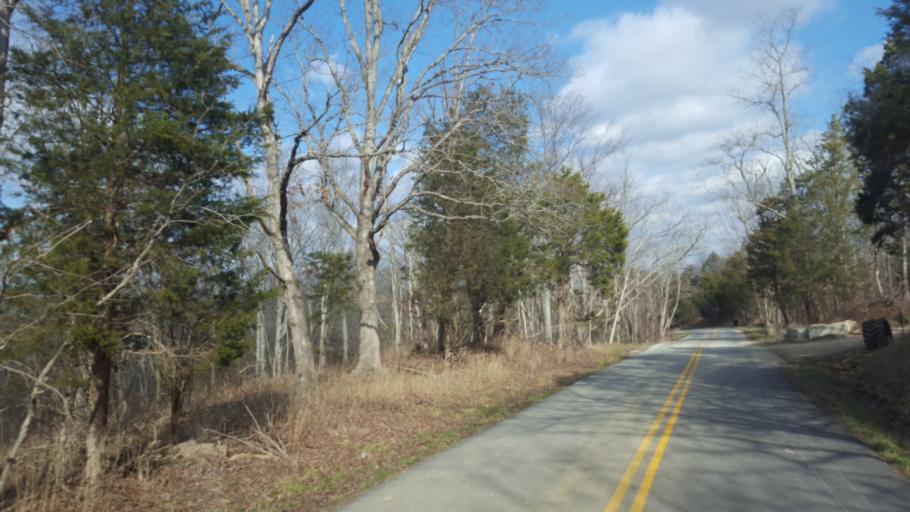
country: US
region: Kentucky
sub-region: Owen County
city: Owenton
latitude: 38.3991
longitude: -84.9591
